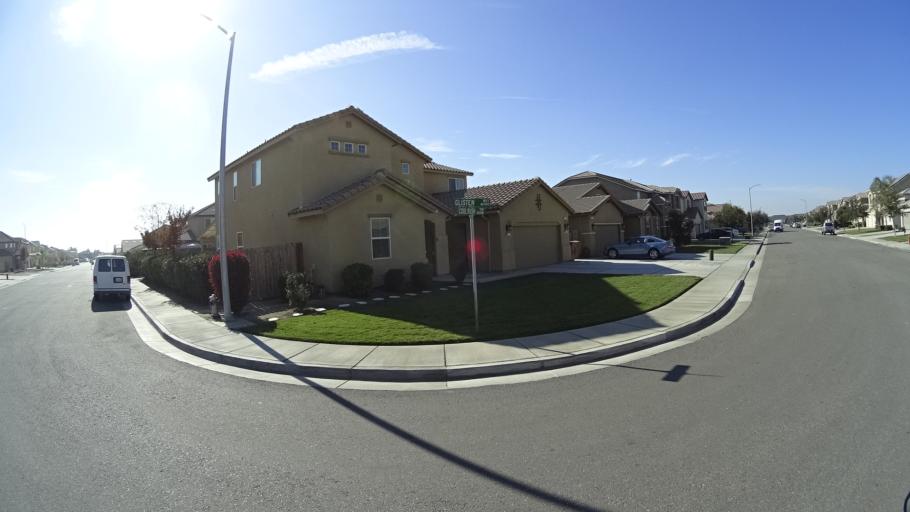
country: US
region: California
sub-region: Kern County
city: Greenfield
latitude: 35.2858
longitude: -119.0578
